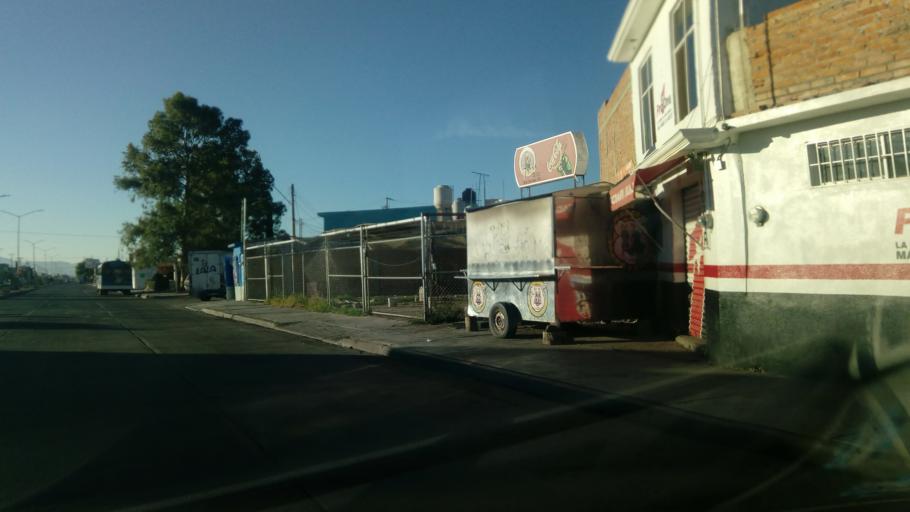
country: MX
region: Durango
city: Victoria de Durango
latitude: 24.0612
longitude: -104.5947
